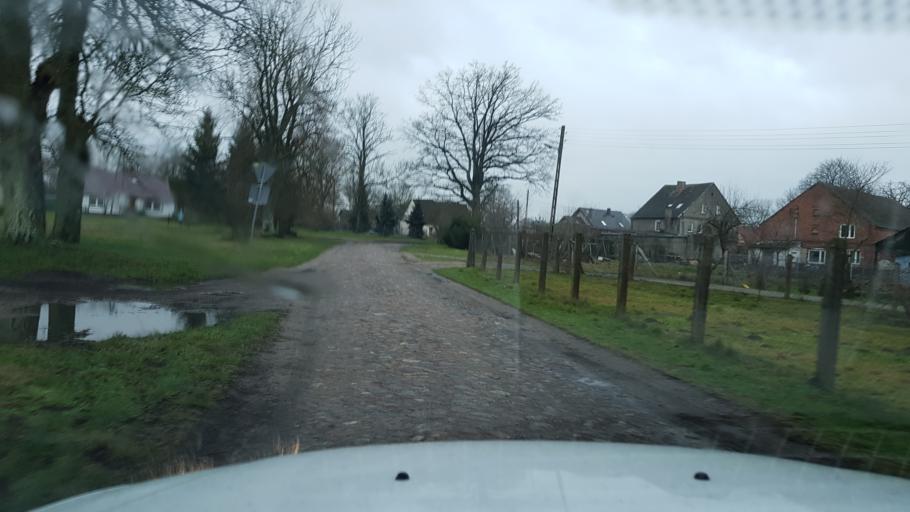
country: PL
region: West Pomeranian Voivodeship
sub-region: Powiat gryficki
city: Brojce
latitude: 53.9913
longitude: 15.3146
